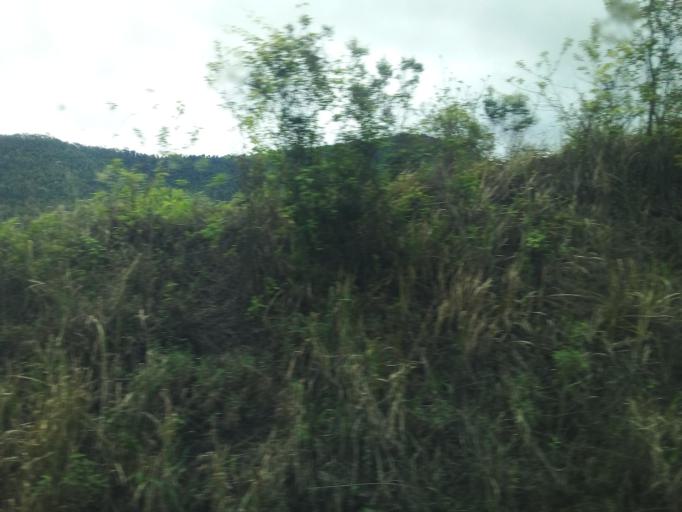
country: BR
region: Minas Gerais
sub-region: Nova Era
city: Nova Era
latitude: -19.6689
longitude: -42.8966
